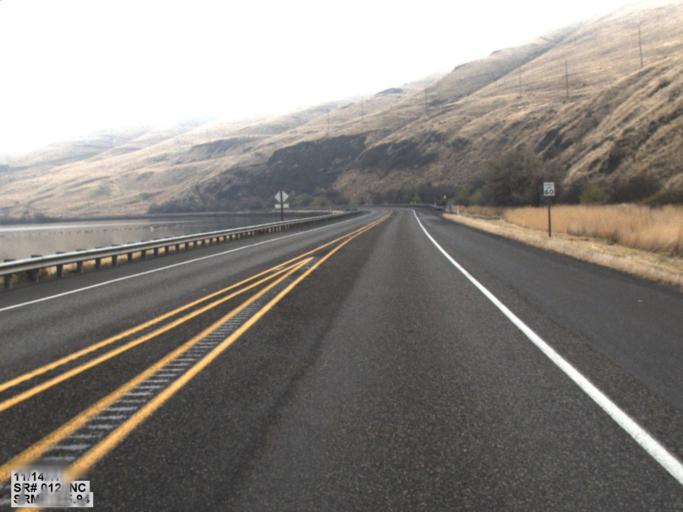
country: US
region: Washington
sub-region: Asotin County
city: Clarkston Heights-Vineland
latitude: 46.4130
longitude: -117.1962
